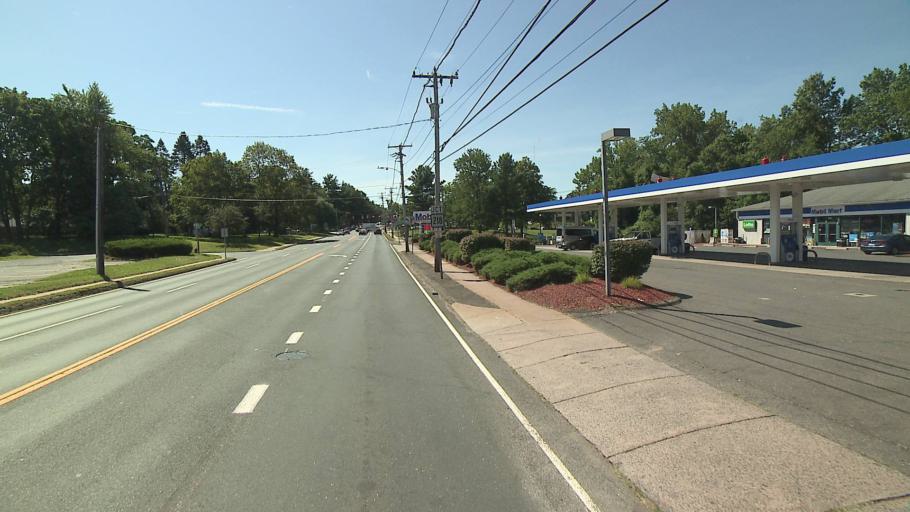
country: US
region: Connecticut
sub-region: Hartford County
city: Blue Hills
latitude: 41.8181
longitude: -72.6955
